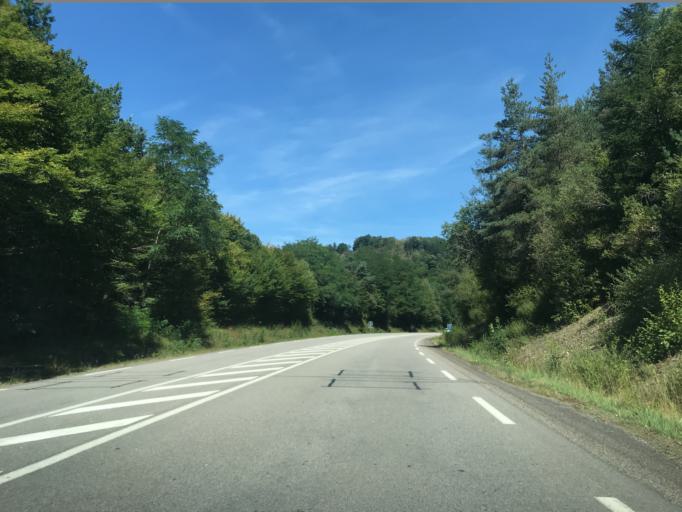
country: FR
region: Limousin
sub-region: Departement de la Correze
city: Laguenne
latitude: 45.2536
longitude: 1.7765
